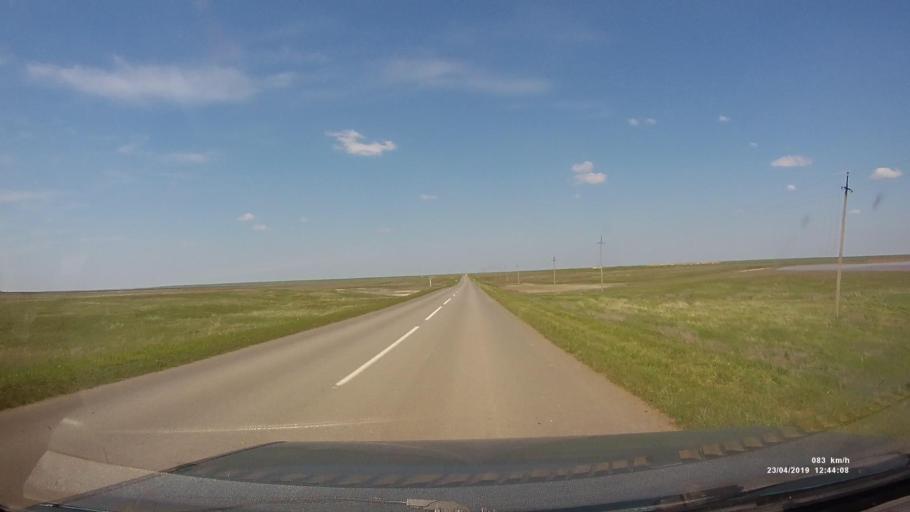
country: RU
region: Kalmykiya
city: Yashalta
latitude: 46.4730
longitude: 42.6489
